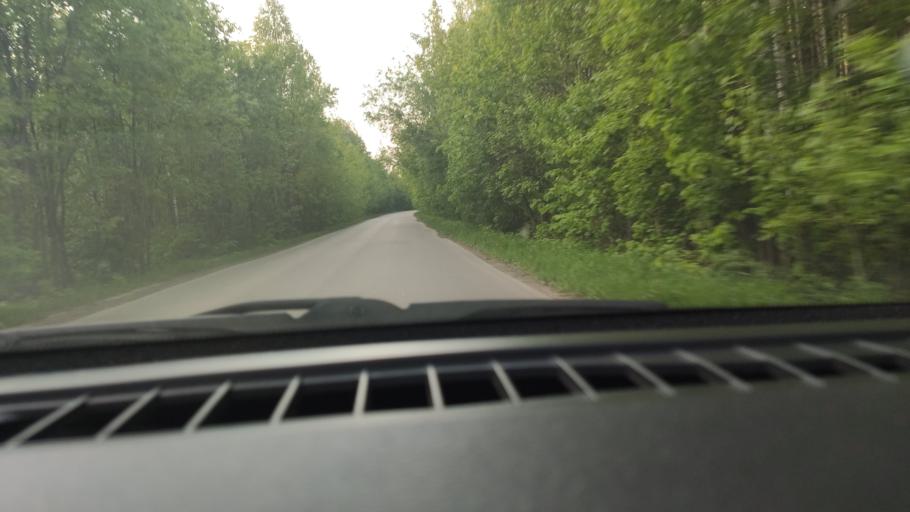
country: RU
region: Perm
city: Kondratovo
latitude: 58.0616
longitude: 56.0034
